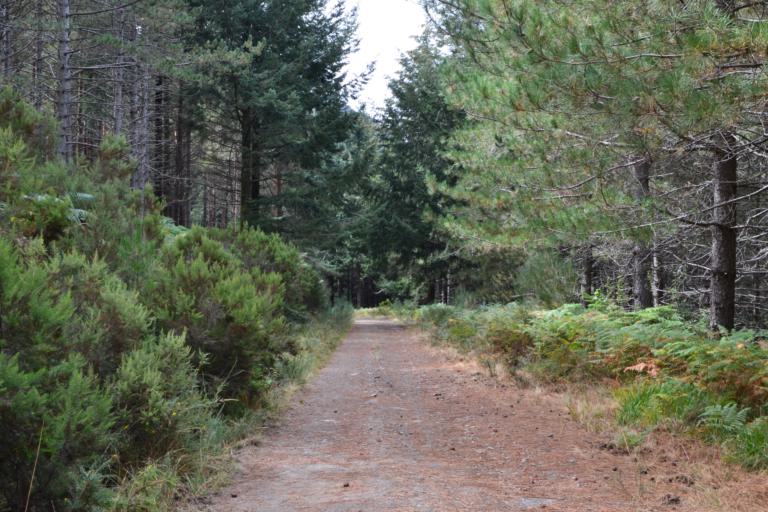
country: PT
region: Vila Real
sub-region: Santa Marta de Penaguiao
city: Santa Marta de Penaguiao
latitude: 41.2766
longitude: -7.8865
